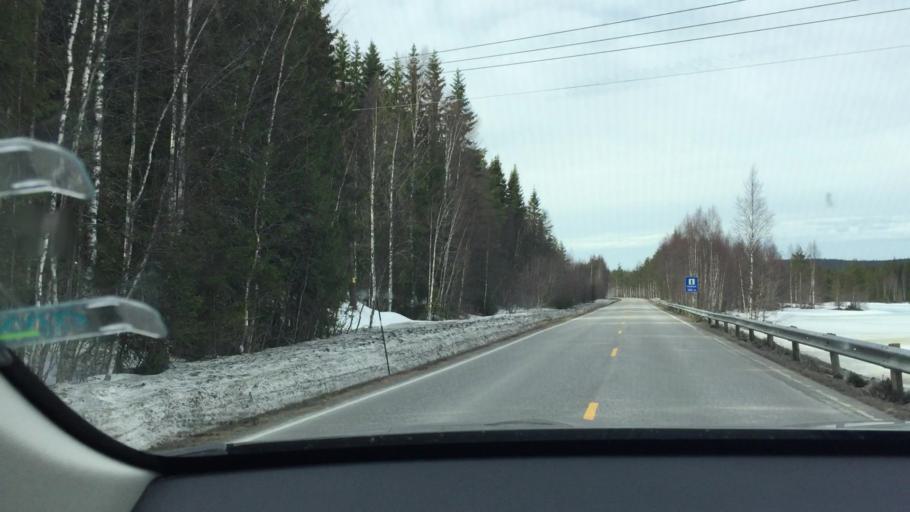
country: NO
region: Hedmark
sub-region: Trysil
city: Innbygda
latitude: 61.0696
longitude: 12.5789
